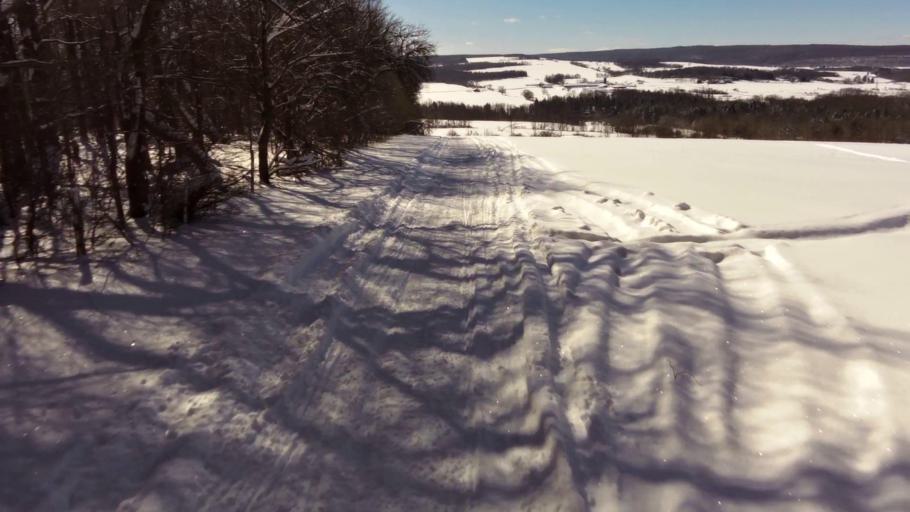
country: US
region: New York
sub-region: Chautauqua County
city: Silver Creek
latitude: 42.3807
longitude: -79.1497
